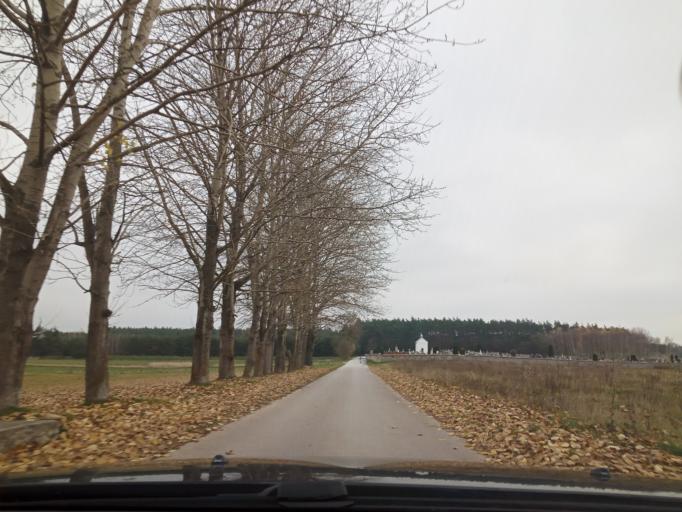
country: PL
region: Swietokrzyskie
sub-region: Powiat jedrzejowski
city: Imielno
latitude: 50.5831
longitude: 20.4507
